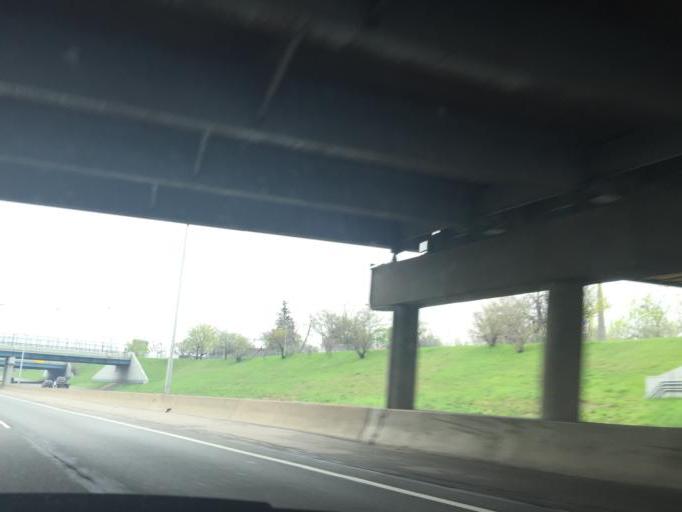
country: US
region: Michigan
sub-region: Wayne County
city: Dearborn
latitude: 42.3830
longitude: -83.1788
